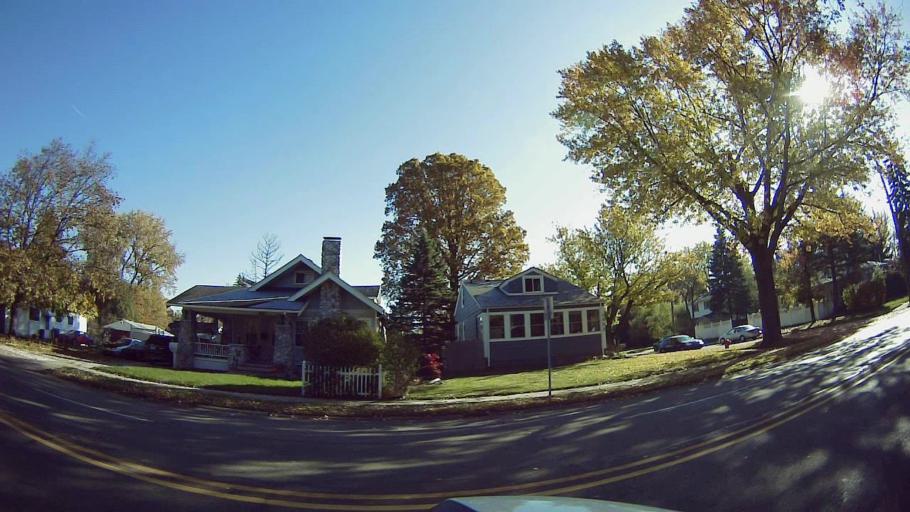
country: US
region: Michigan
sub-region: Oakland County
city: Clawson
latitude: 42.5211
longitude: -83.1457
